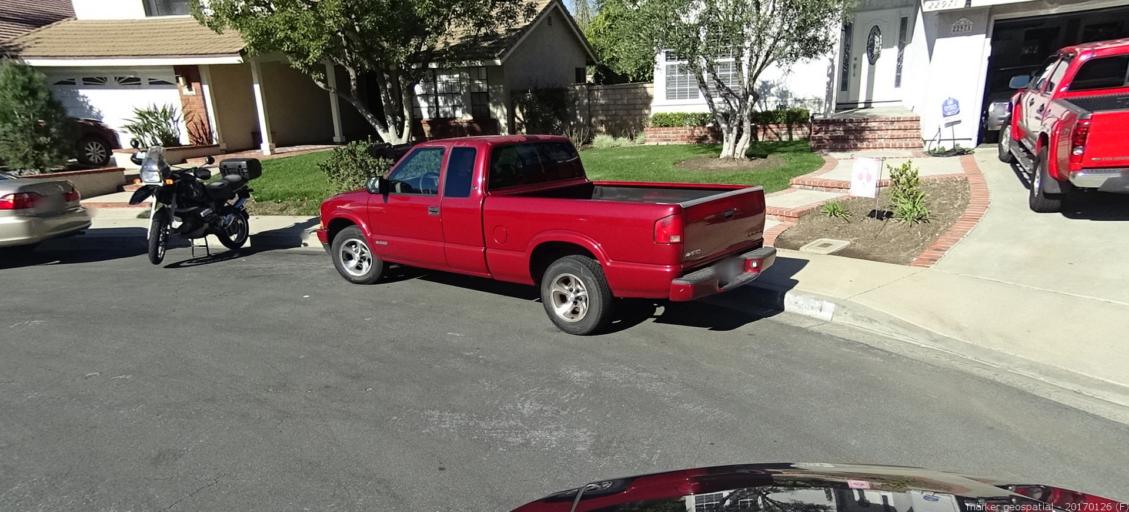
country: US
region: California
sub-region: Orange County
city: Lake Forest
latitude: 33.6291
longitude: -117.6852
